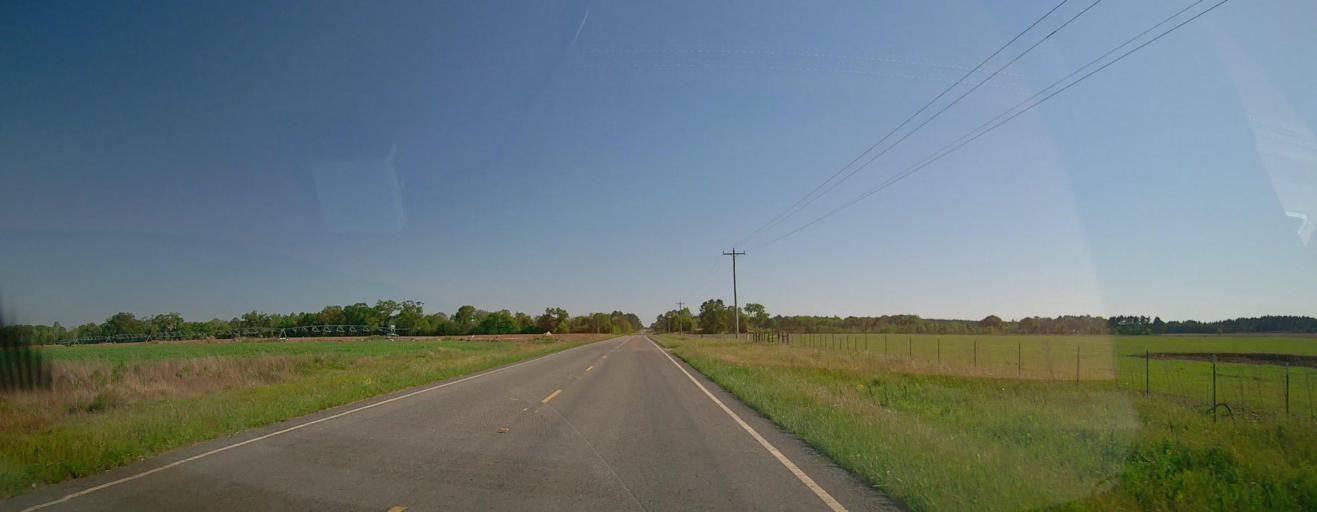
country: US
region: Georgia
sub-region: Wilcox County
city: Rochelle
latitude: 32.0727
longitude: -83.5035
